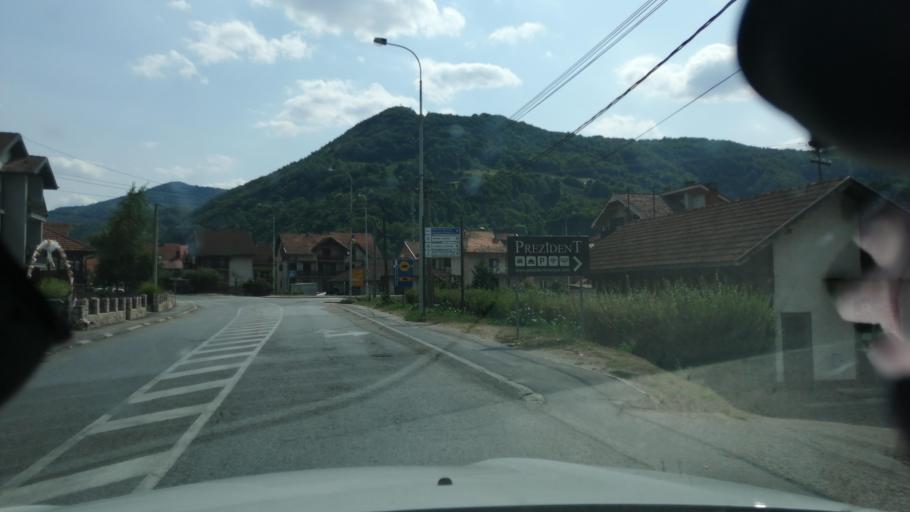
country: RS
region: Central Serbia
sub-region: Moravicki Okrug
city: Ivanjica
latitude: 43.5992
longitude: 20.2239
